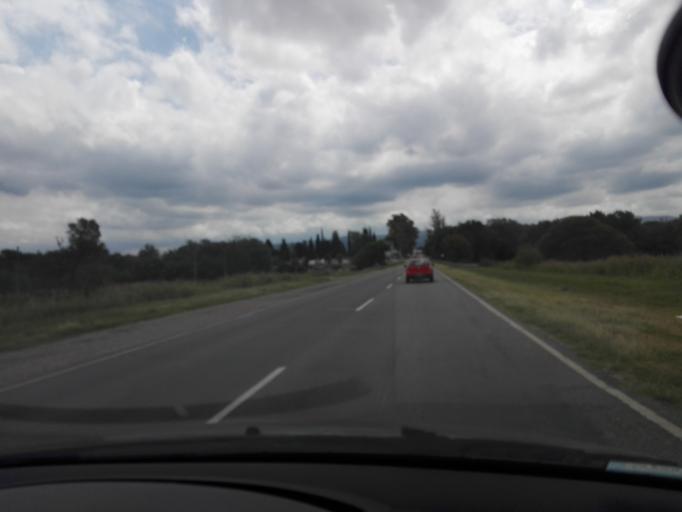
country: AR
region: Cordoba
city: Alta Gracia
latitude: -31.6583
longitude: -64.4024
